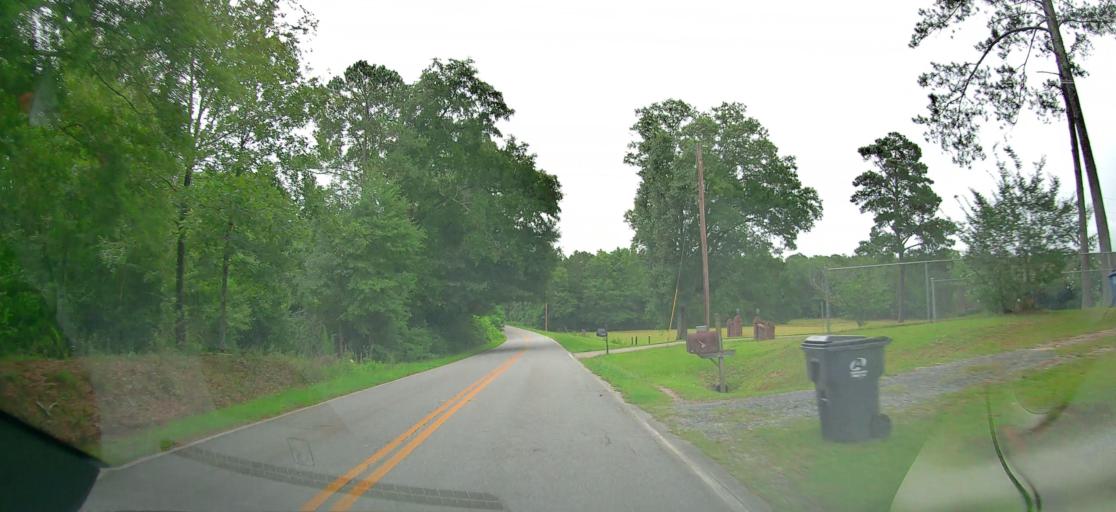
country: US
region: Georgia
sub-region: Bibb County
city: West Point
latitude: 32.7627
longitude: -83.7893
